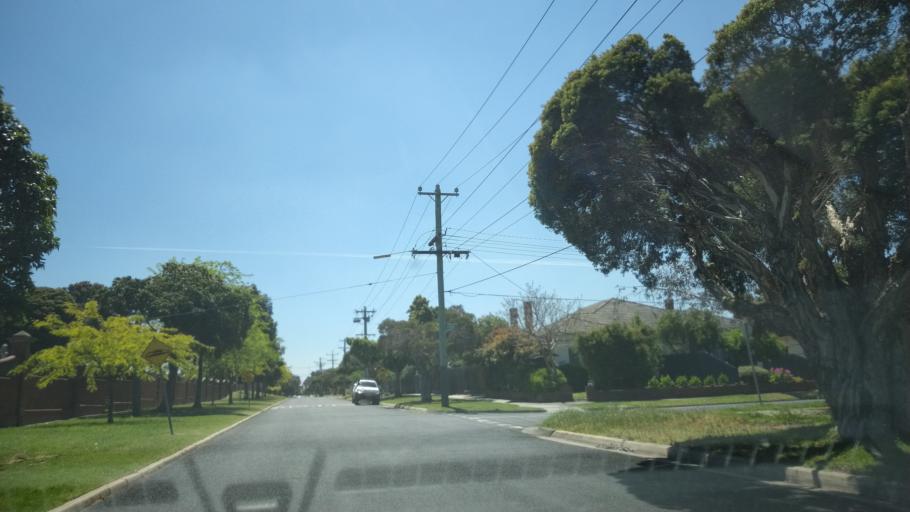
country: AU
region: Victoria
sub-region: Glen Eira
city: Caulfield South
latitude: -37.8994
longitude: 145.0232
